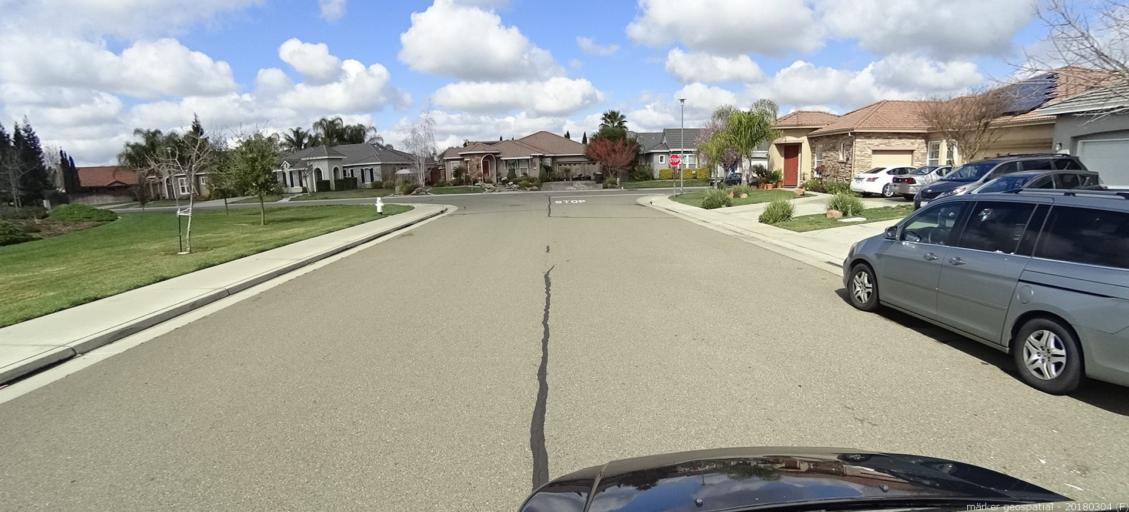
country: US
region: California
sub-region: Sacramento County
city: Vineyard
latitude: 38.4569
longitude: -121.3243
